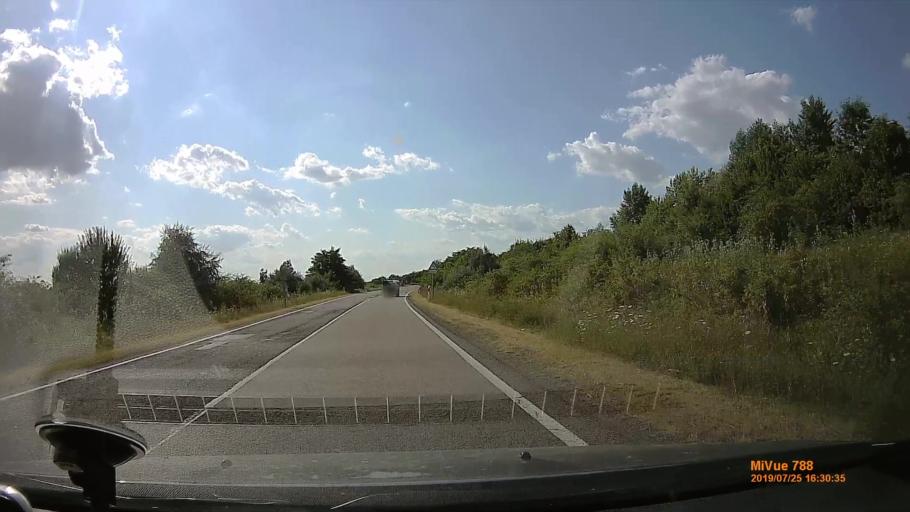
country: HU
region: Heves
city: Karacsond
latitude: 47.7298
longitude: 20.0519
